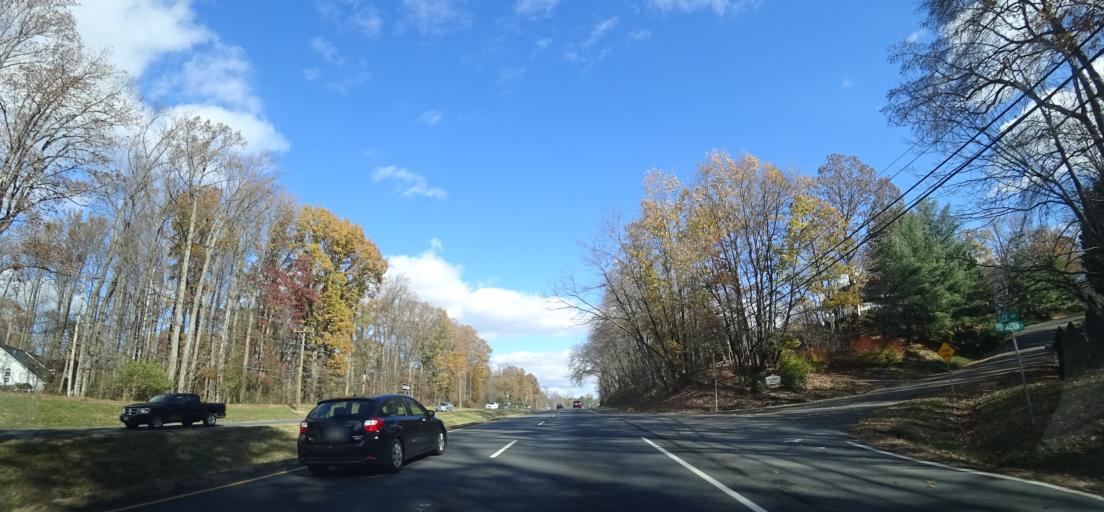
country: US
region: Virginia
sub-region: Fauquier County
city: New Baltimore
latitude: 38.7565
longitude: -77.7413
